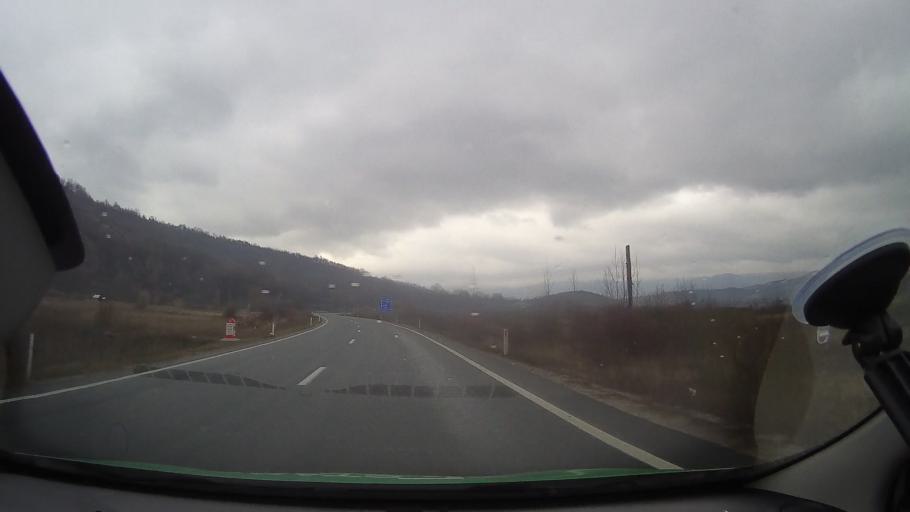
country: RO
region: Hunedoara
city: Vata de Jos
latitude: 46.2145
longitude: 22.5774
